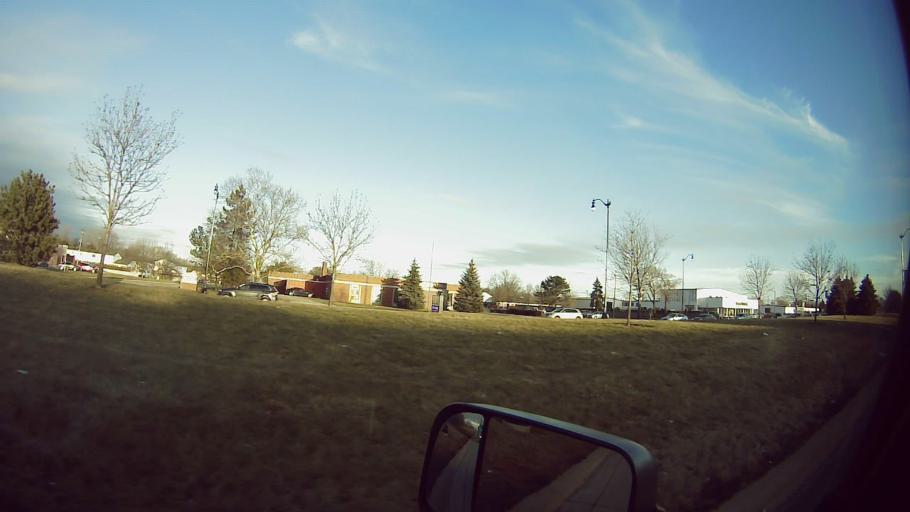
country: US
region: Michigan
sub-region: Wayne County
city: Taylor
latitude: 42.2304
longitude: -83.2695
